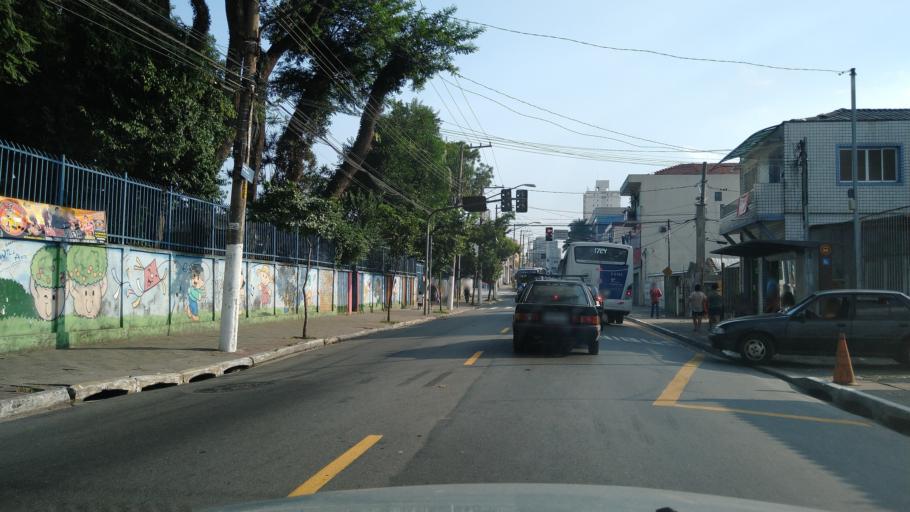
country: BR
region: Sao Paulo
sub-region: Guarulhos
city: Guarulhos
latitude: -23.4794
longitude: -46.5843
